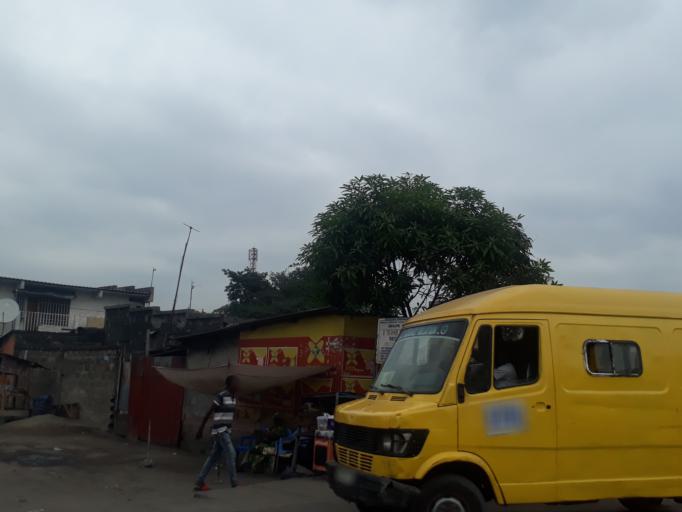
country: CD
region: Kinshasa
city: Kinshasa
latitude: -4.3210
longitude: 15.3116
